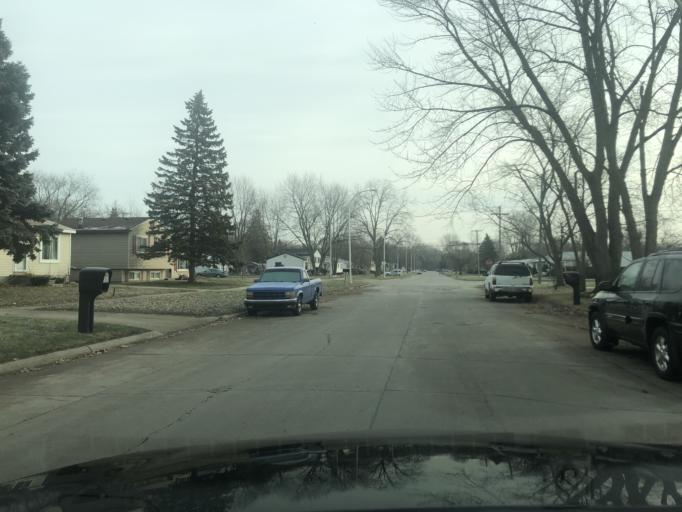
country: US
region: Michigan
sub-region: Wayne County
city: Taylor
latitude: 42.1880
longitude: -83.3166
